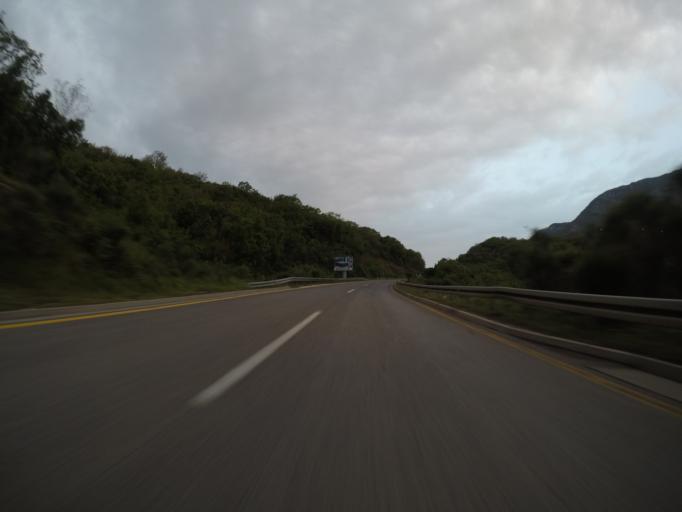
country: ME
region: Bar
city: Sutomore
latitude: 42.1563
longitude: 19.0268
